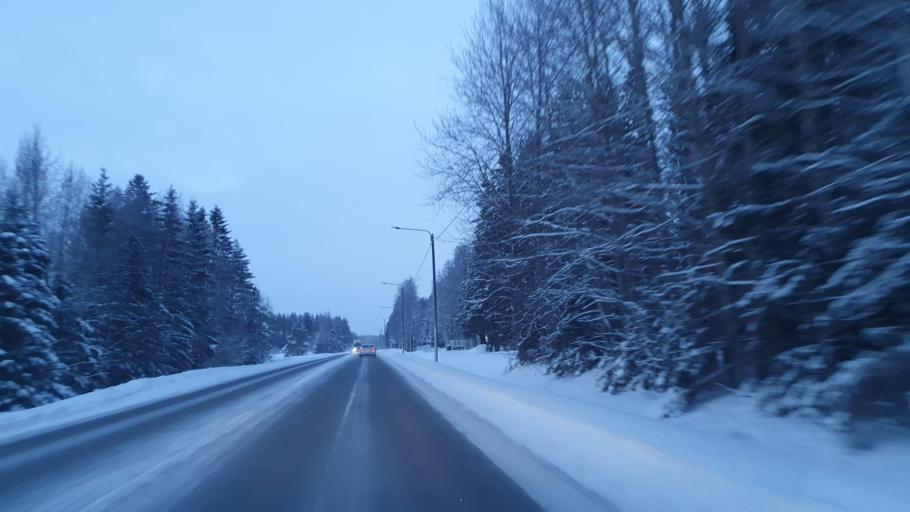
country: FI
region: Northern Ostrobothnia
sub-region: Oulu
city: Muhos
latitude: 64.8288
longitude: 25.9238
